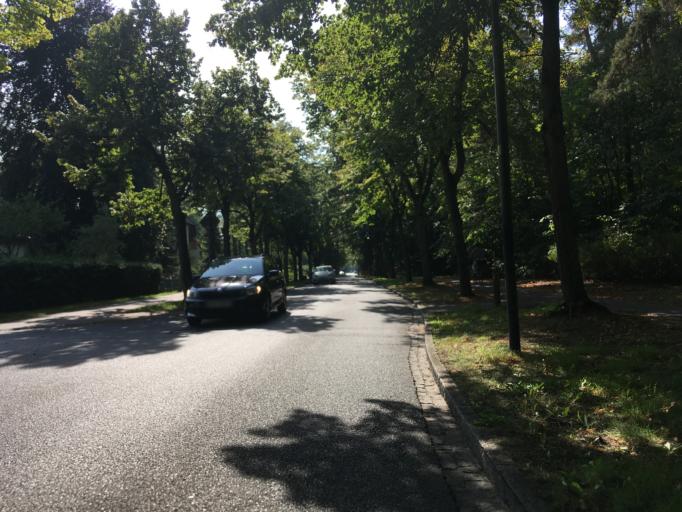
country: DE
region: Brandenburg
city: Zeuthen
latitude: 52.3645
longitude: 13.6251
